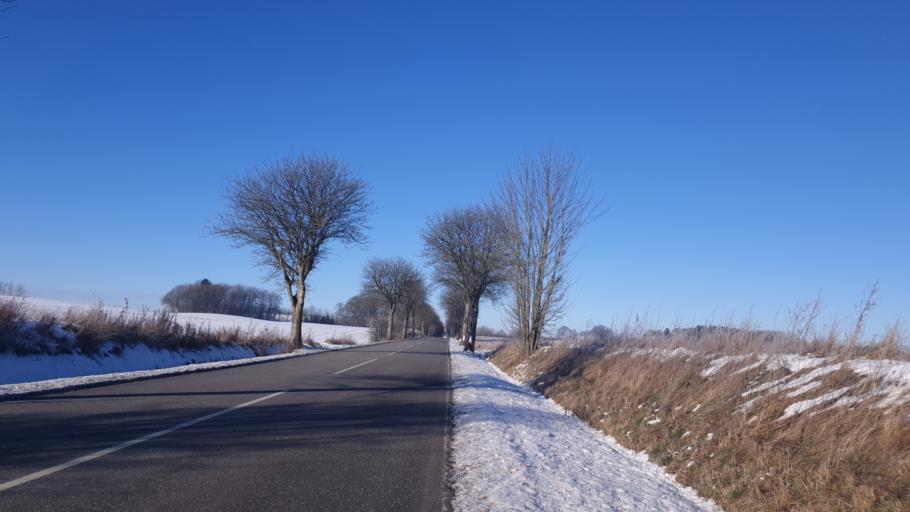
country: DK
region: Central Jutland
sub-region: Hedensted Kommune
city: Hedensted
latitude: 55.7973
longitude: 9.7418
